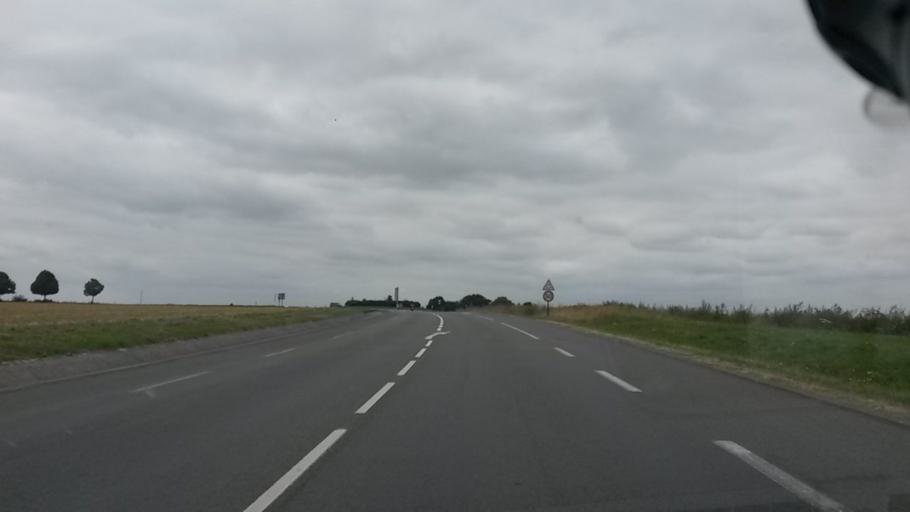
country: FR
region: Nord-Pas-de-Calais
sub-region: Departement du Pas-de-Calais
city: Bapaume
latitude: 50.1150
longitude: 2.8488
